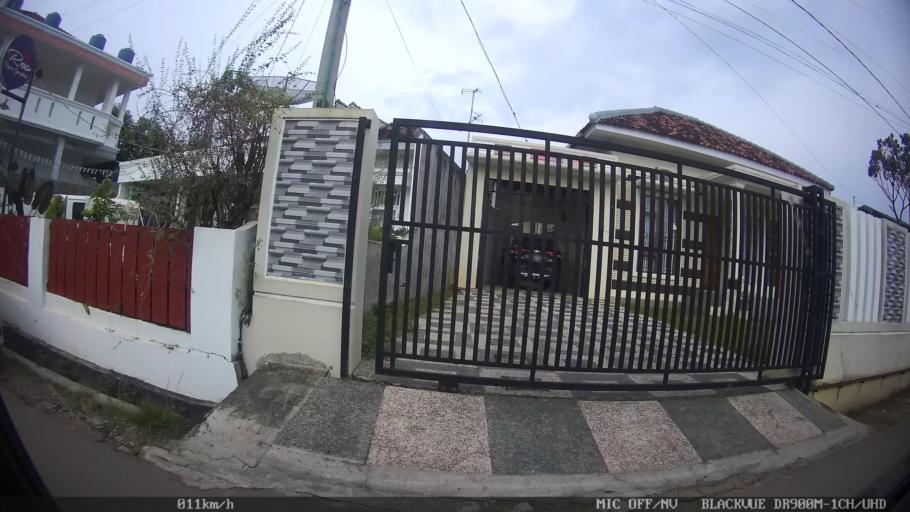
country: ID
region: Lampung
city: Kedaton
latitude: -5.3928
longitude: 105.2323
